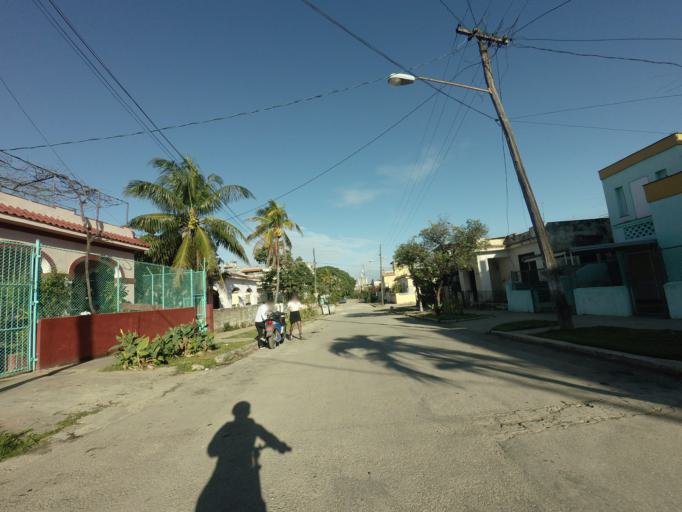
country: CU
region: La Habana
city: Cerro
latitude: 23.1026
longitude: -82.4322
